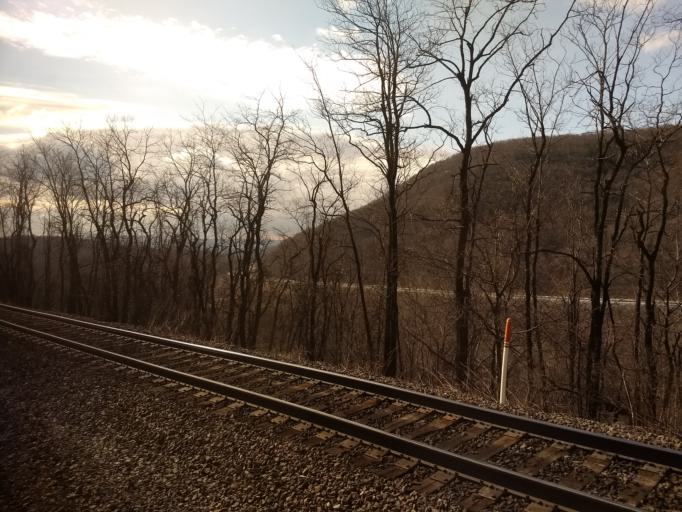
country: US
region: Pennsylvania
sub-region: Cambria County
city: Gallitzin
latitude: 40.4754
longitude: -78.4904
